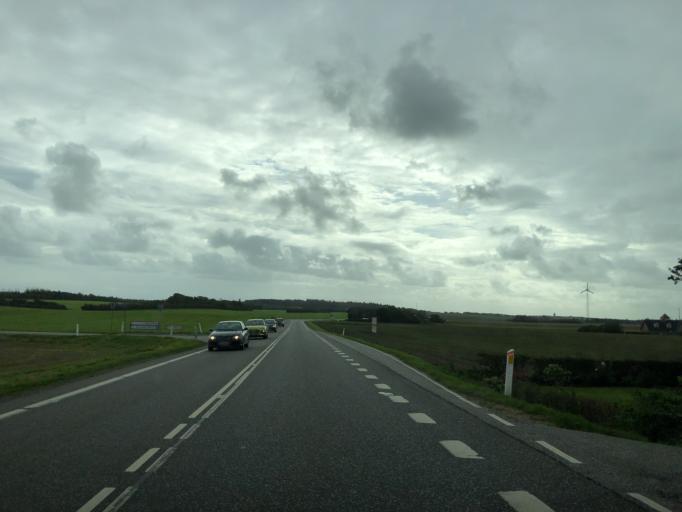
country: DK
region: North Denmark
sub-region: Thisted Kommune
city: Hurup
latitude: 56.7292
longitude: 8.4288
